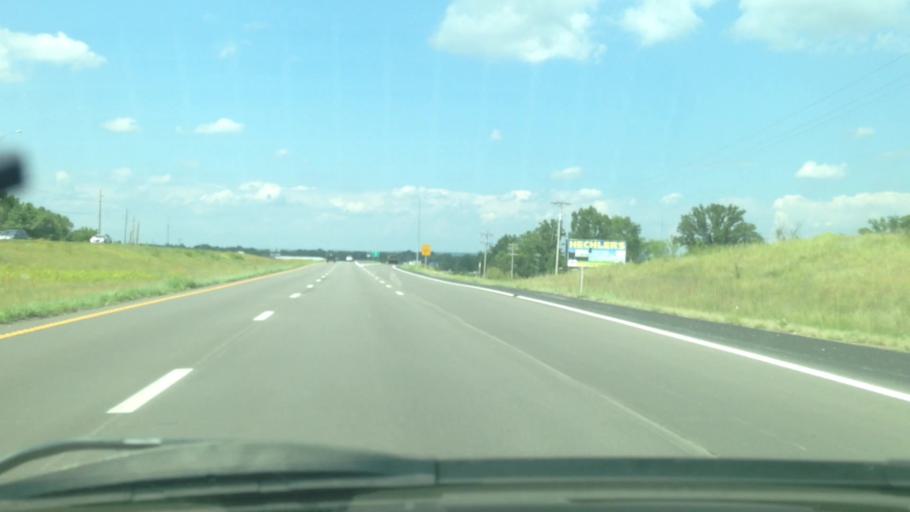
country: US
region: Missouri
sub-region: Lincoln County
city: Moscow Mills
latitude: 38.9412
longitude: -90.9259
